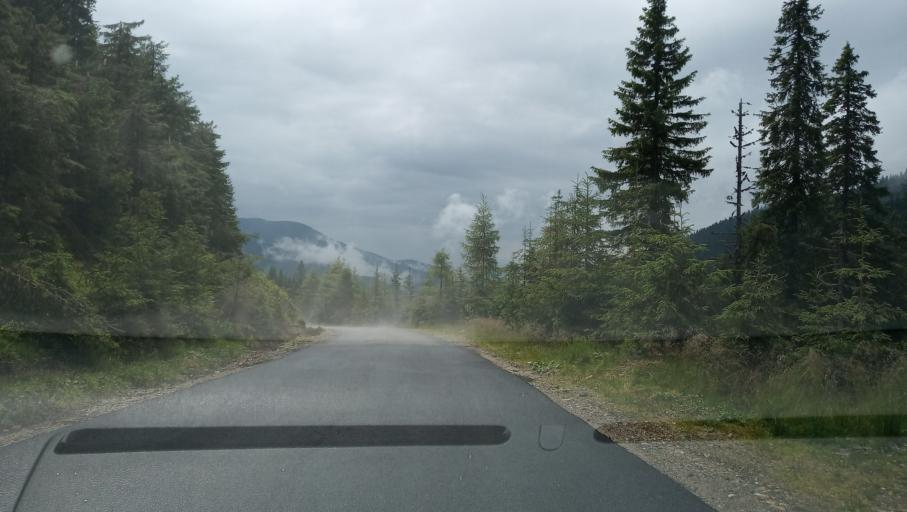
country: RO
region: Hunedoara
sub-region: Oras Petrila
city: Petrila
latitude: 45.4132
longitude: 23.5907
